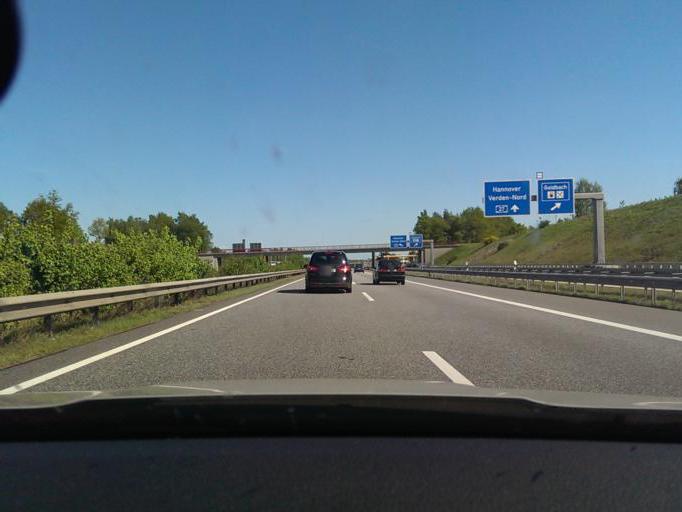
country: DE
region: Lower Saxony
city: Langwedel
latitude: 53.0016
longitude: 9.1753
